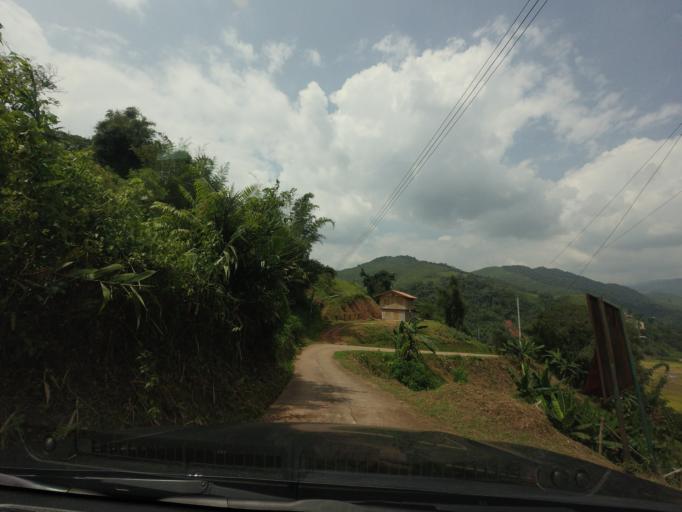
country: TH
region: Nan
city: Bo Kluea
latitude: 19.1891
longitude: 101.2006
